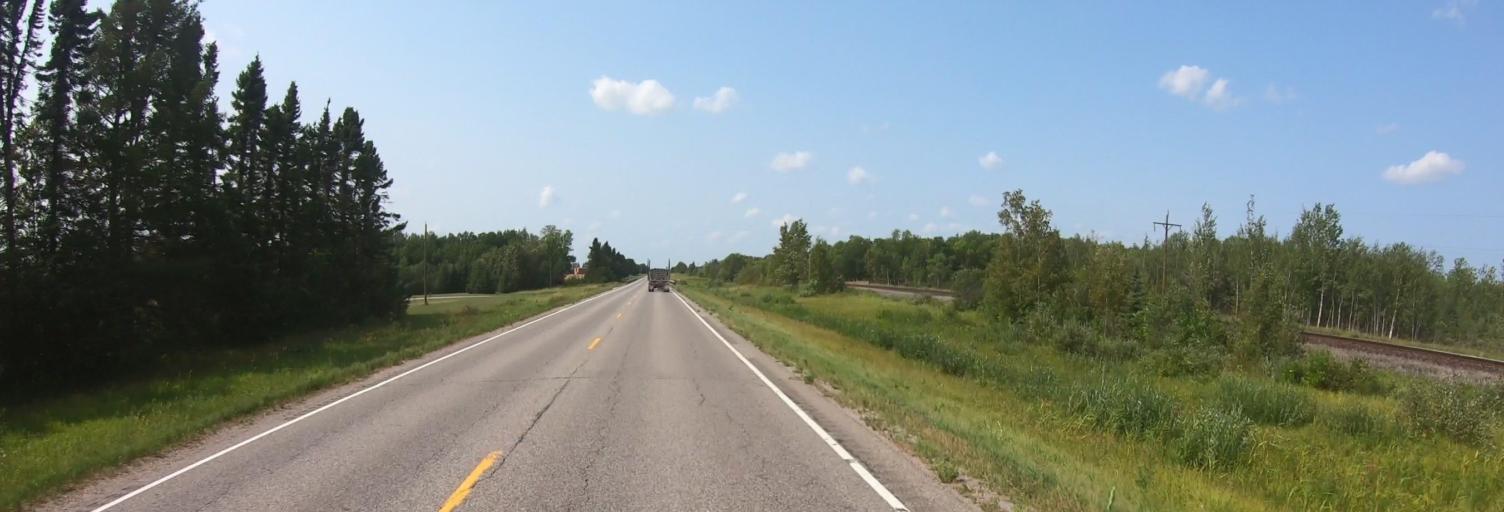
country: US
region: Minnesota
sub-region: Roseau County
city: Warroad
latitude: 48.8205
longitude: -95.1417
